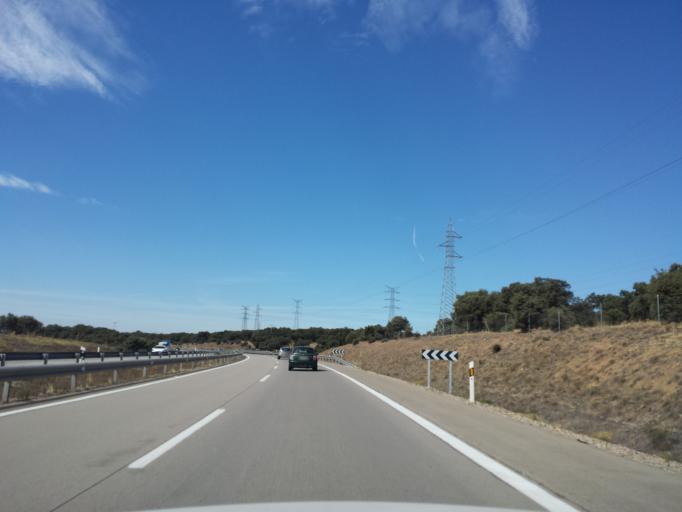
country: ES
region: Castille-La Mancha
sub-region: Province of Toledo
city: Mejorada
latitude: 39.9717
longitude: -4.8897
